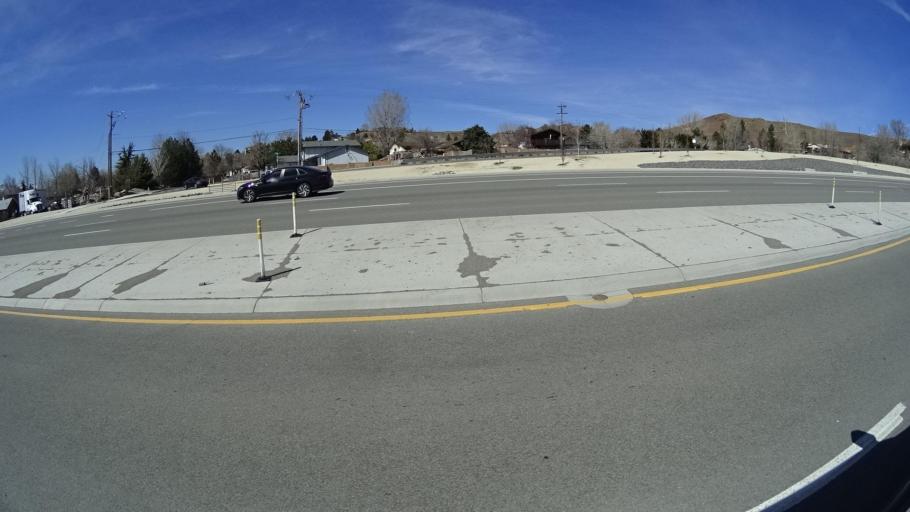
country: US
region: Nevada
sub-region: Washoe County
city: Sparks
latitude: 39.5607
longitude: -119.7519
